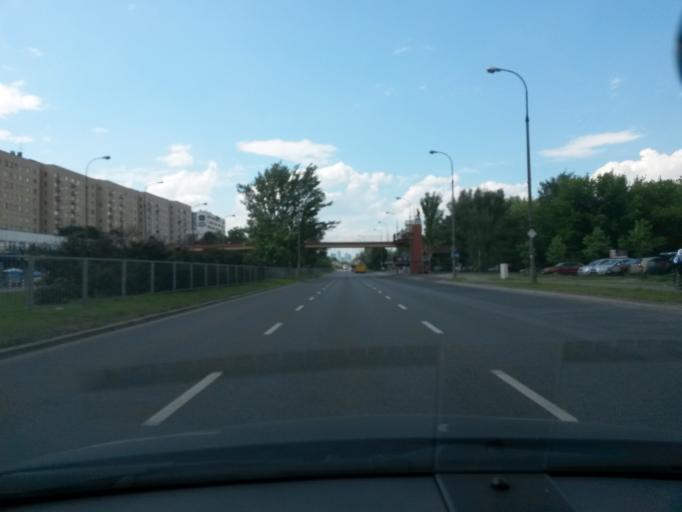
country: PL
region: Masovian Voivodeship
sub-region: Warszawa
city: Mokotow
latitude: 52.1847
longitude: 21.0529
